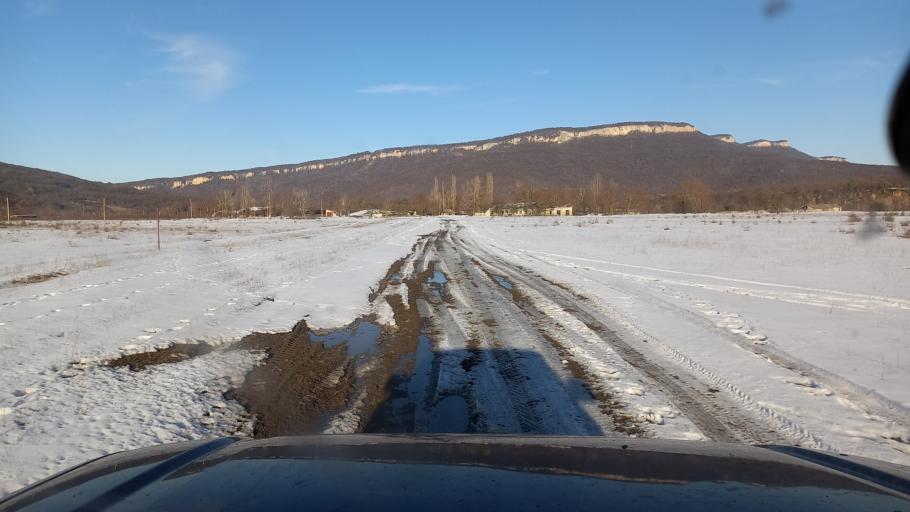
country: RU
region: Adygeya
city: Kamennomostskiy
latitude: 44.2197
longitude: 40.1805
